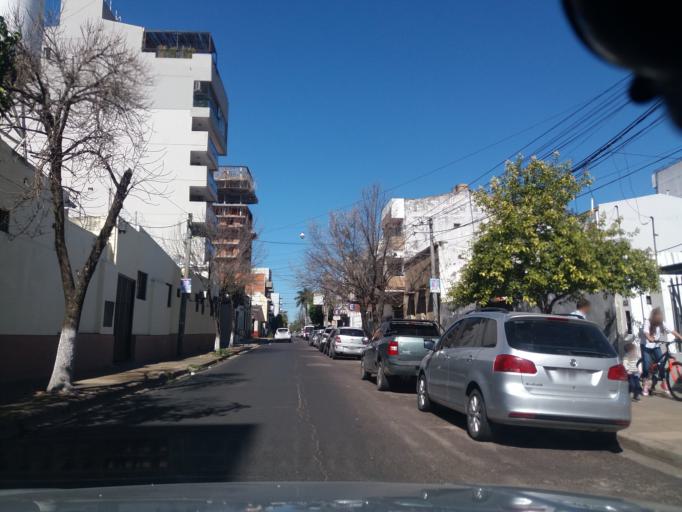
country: AR
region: Corrientes
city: Corrientes
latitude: -27.4697
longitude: -58.8418
